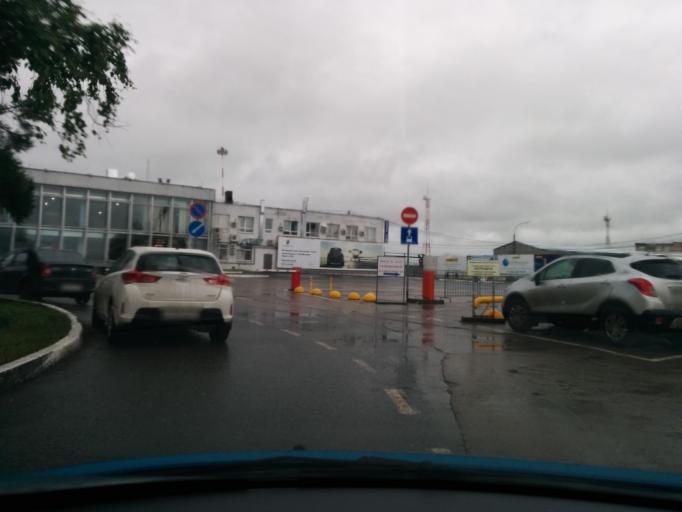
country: RU
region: Perm
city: Kultayevo
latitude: 57.9201
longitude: 56.0185
